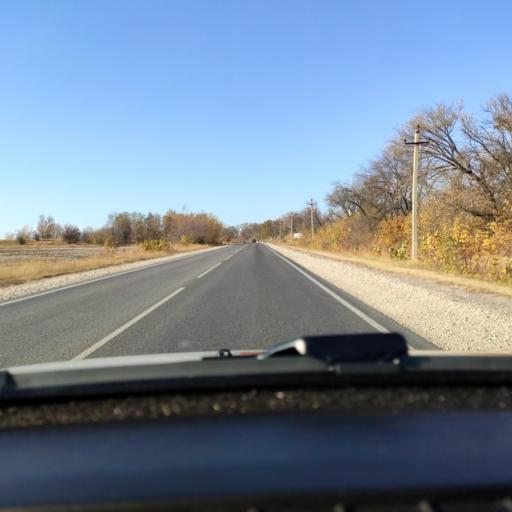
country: RU
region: Voronezj
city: Semiluki
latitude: 51.7262
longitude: 38.9891
